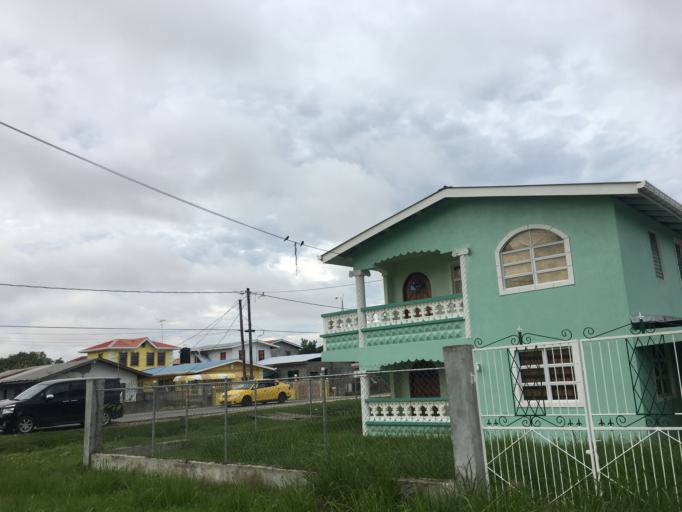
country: GY
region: Demerara-Mahaica
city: Georgetown
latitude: 6.8060
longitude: -58.1189
